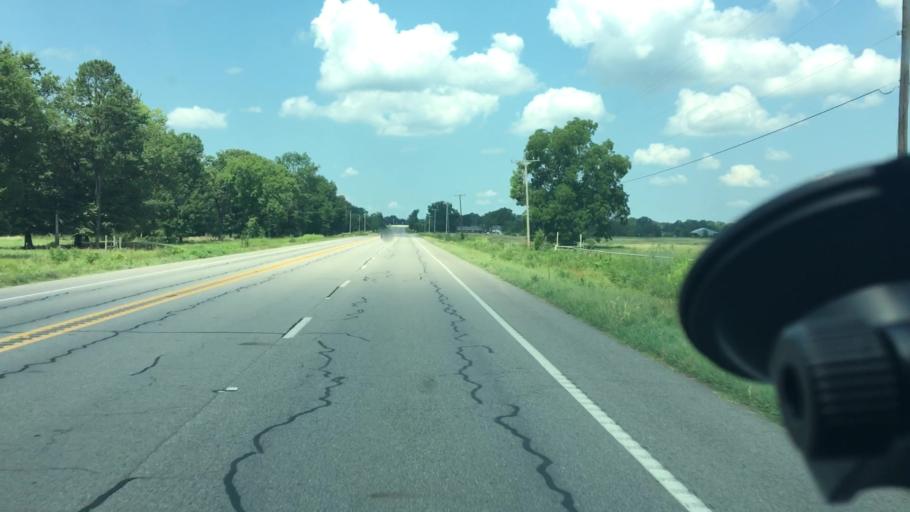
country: US
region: Arkansas
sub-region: Logan County
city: Paris
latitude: 35.2986
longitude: -93.8167
